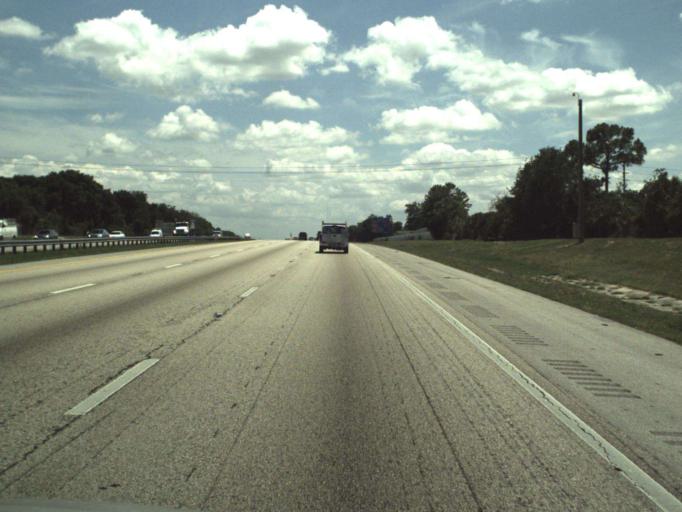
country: US
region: Florida
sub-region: Seminole County
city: Altamonte Springs
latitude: 28.6486
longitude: -81.3887
